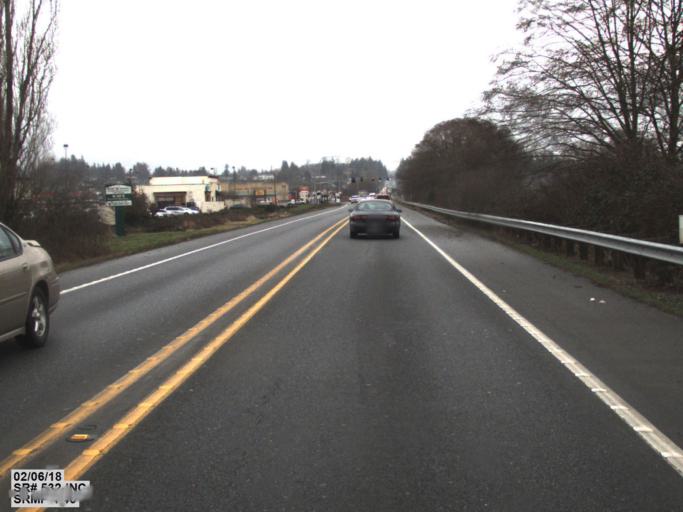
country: US
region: Washington
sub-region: Snohomish County
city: Stanwood
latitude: 48.2399
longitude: -122.3614
